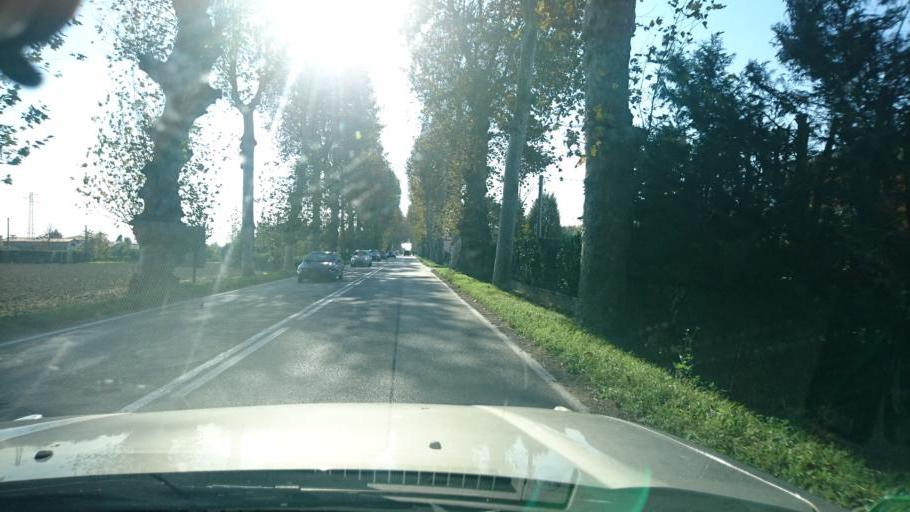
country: IT
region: Veneto
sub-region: Provincia di Padova
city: Monselice
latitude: 45.2288
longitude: 11.7549
